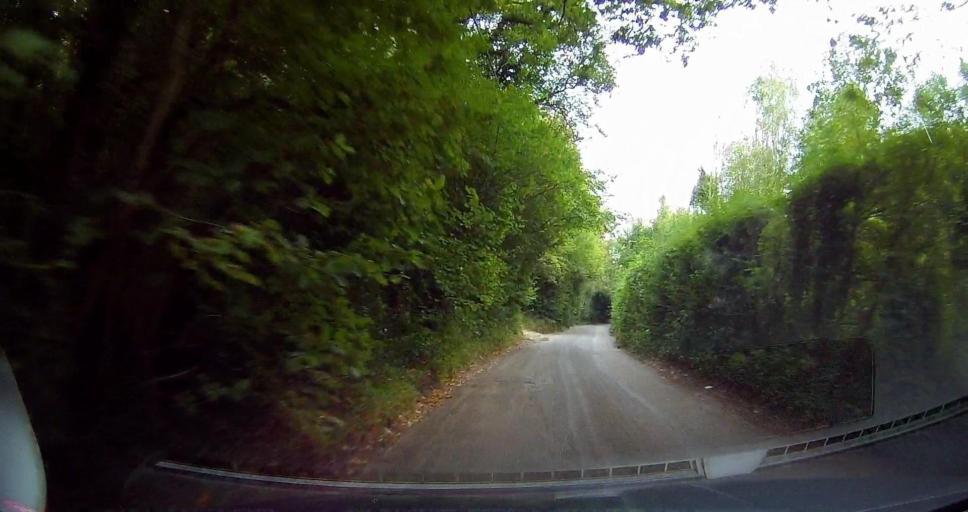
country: GB
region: England
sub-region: Kent
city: Longfield
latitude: 51.3625
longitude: 0.2812
